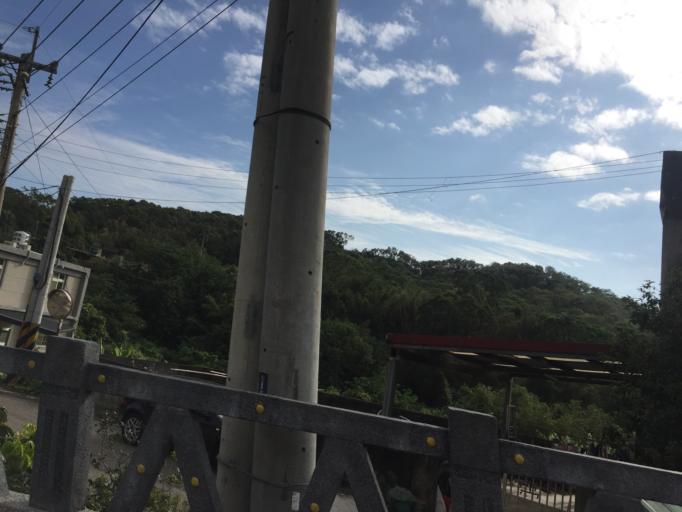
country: TW
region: Taiwan
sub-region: Hsinchu
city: Hsinchu
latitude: 24.7738
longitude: 120.9497
